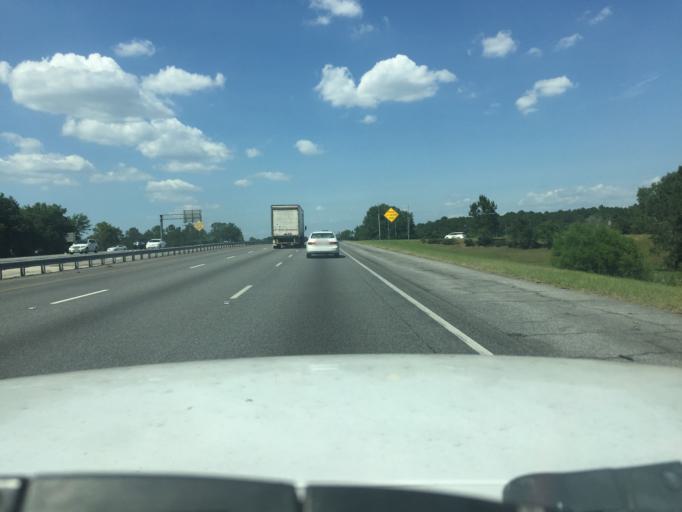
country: US
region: Georgia
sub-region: Chatham County
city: Pooler
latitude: 32.0719
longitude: -81.2470
